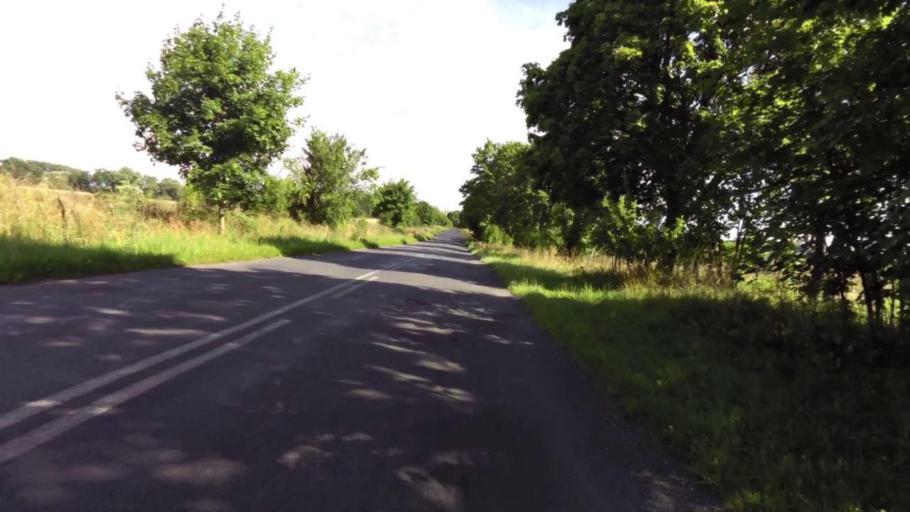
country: PL
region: West Pomeranian Voivodeship
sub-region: Powiat stargardzki
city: Dobrzany
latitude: 53.3749
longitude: 15.4348
